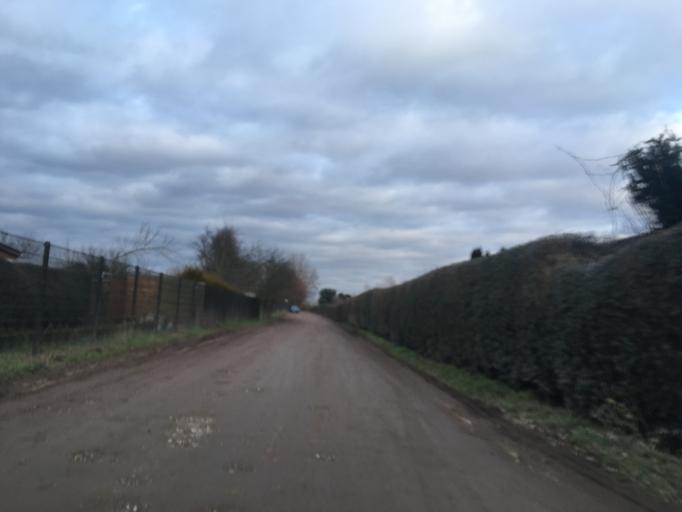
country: DE
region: Berlin
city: Karow
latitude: 52.6205
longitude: 13.4725
